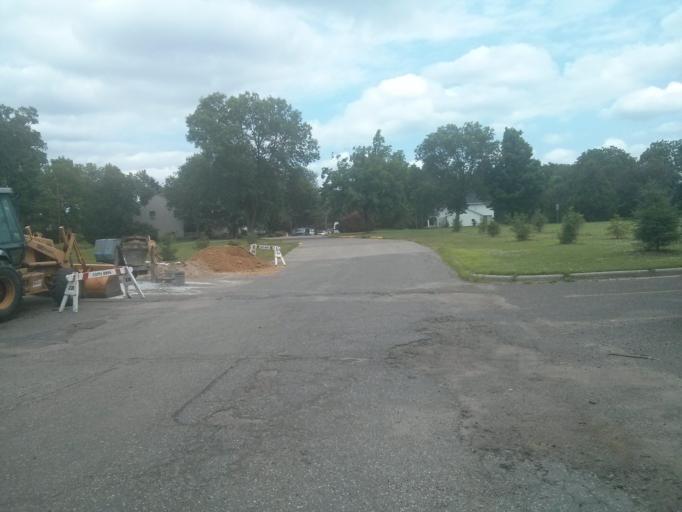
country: US
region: Wisconsin
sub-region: Saint Croix County
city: Hudson
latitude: 44.9724
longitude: -92.7530
